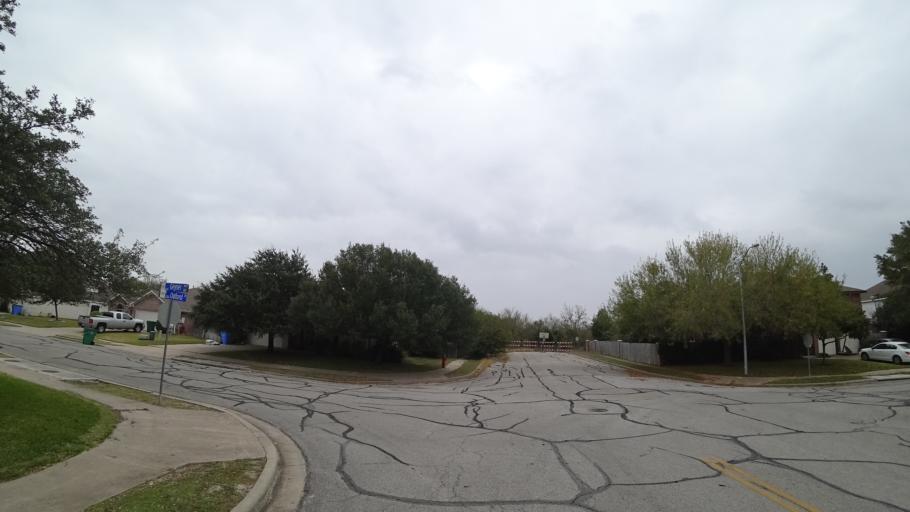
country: US
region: Texas
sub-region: Travis County
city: Pflugerville
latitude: 30.4337
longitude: -97.6218
